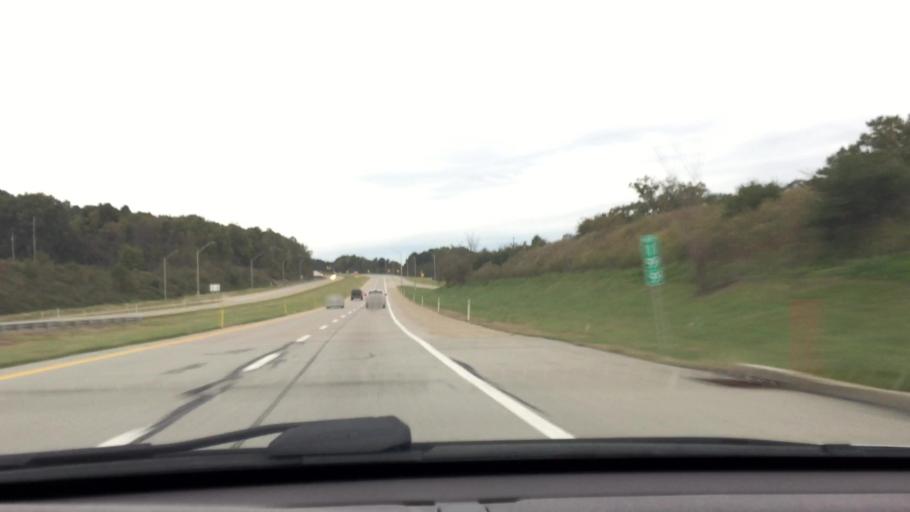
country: US
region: Pennsylvania
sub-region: Lawrence County
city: New Beaver
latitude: 40.9194
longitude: -80.3852
